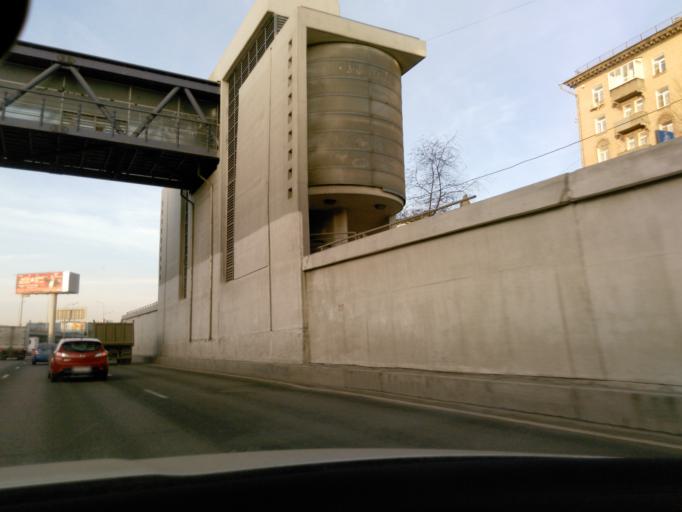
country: RU
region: Moskovskaya
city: Kozhukhovo
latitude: 55.7045
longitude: 37.6593
